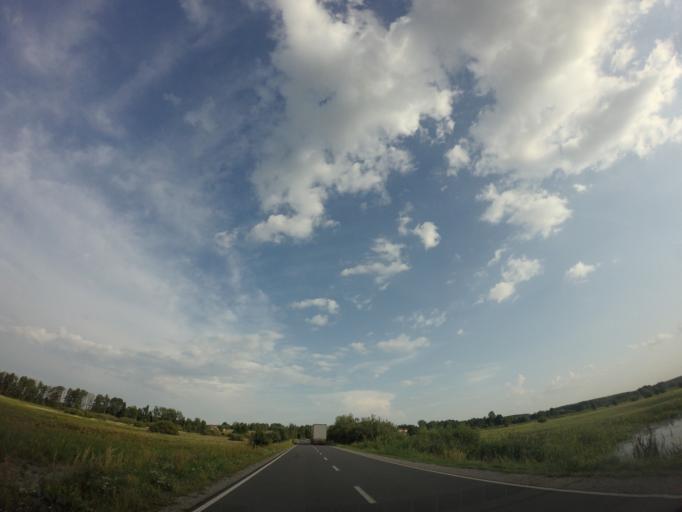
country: PL
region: Lublin Voivodeship
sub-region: Powiat lubartowski
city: Jeziorzany
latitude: 51.5937
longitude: 22.2808
